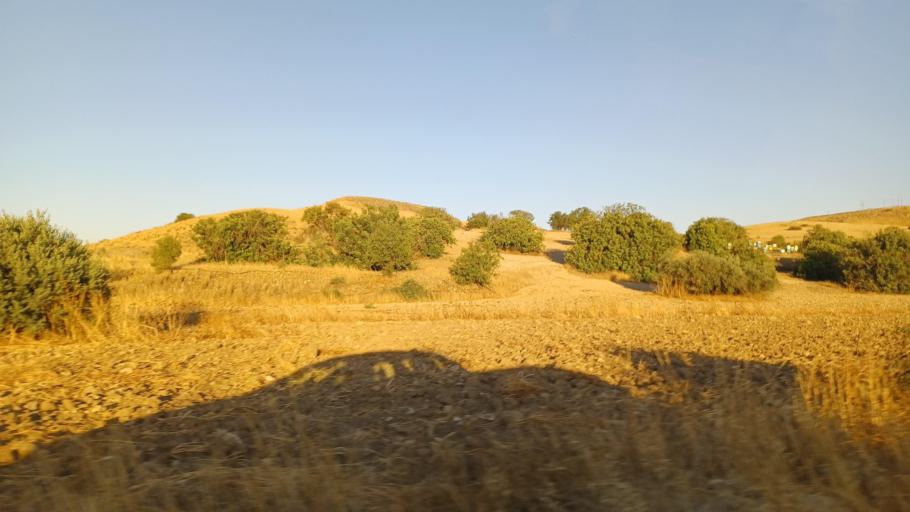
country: CY
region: Larnaka
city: Troulloi
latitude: 35.0260
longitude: 33.6314
